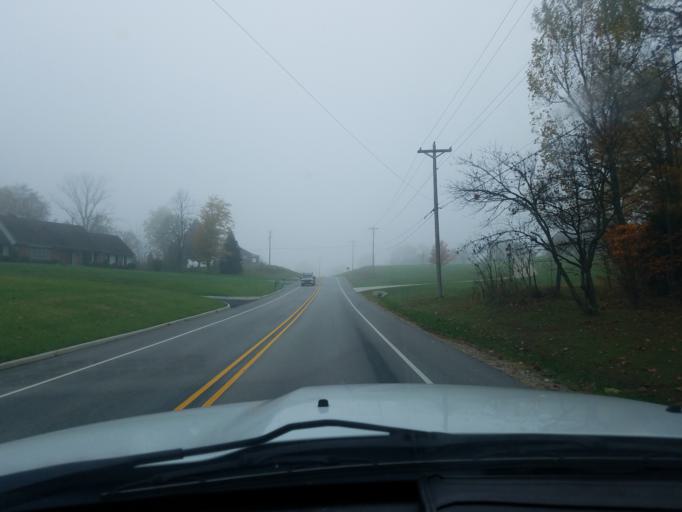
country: US
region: Indiana
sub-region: Floyd County
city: Galena
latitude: 38.3220
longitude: -85.9091
